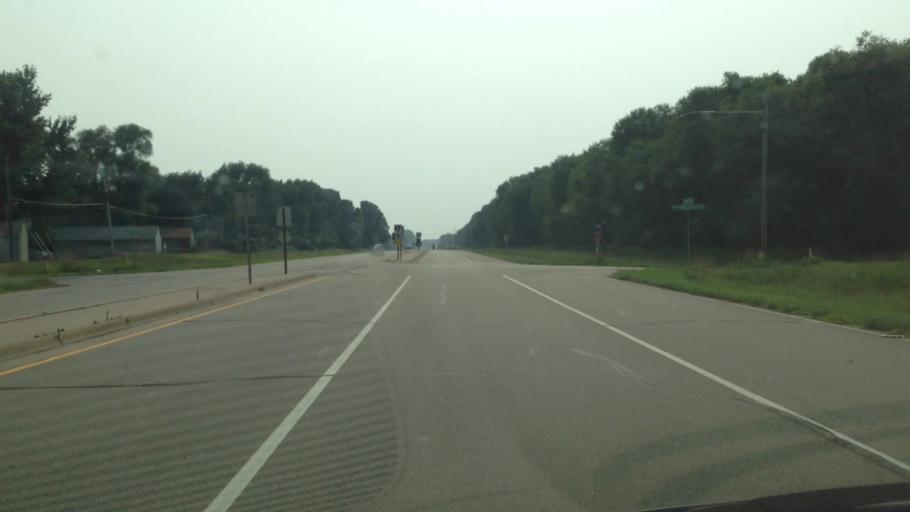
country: US
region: Minnesota
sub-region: Anoka County
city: Circle Pines
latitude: 45.1514
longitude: -93.1406
